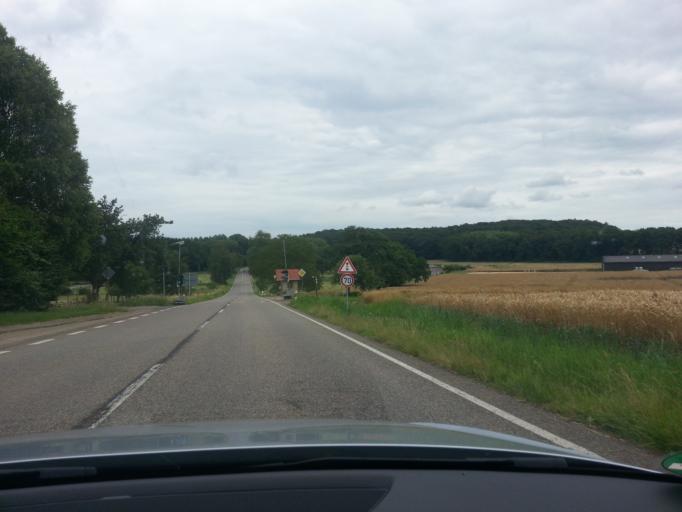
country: DE
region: Saarland
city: Perl
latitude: 49.4941
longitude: 6.4352
